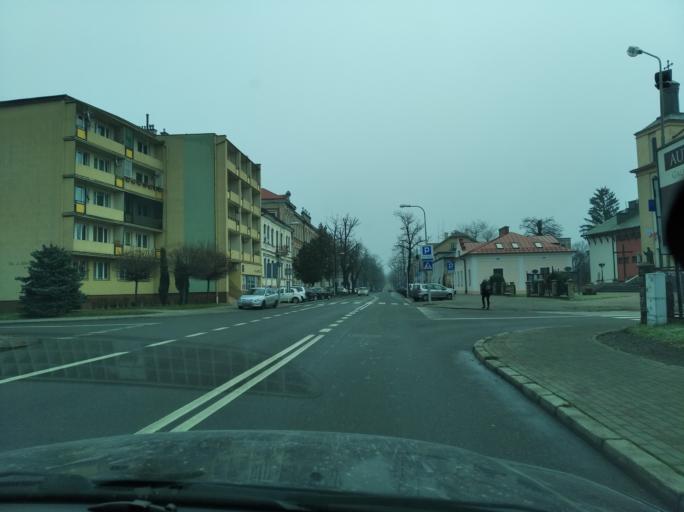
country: PL
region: Subcarpathian Voivodeship
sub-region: Rzeszow
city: Rzeszow
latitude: 50.0418
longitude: 21.9916
